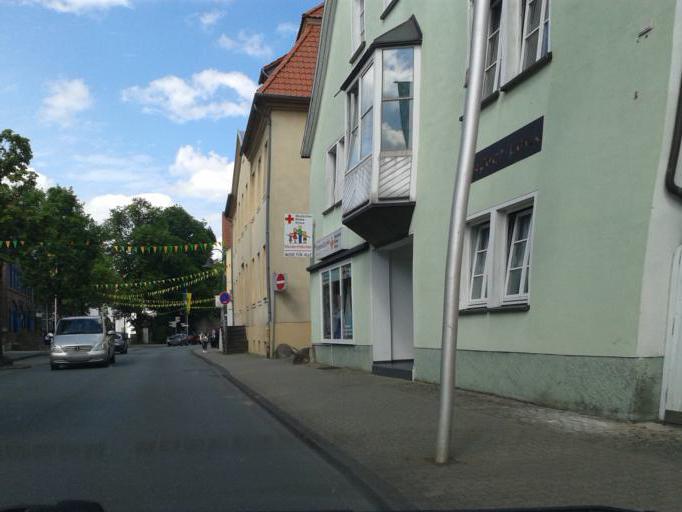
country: DE
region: North Rhine-Westphalia
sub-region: Regierungsbezirk Detmold
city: Paderborn
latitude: 51.7435
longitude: 8.7117
